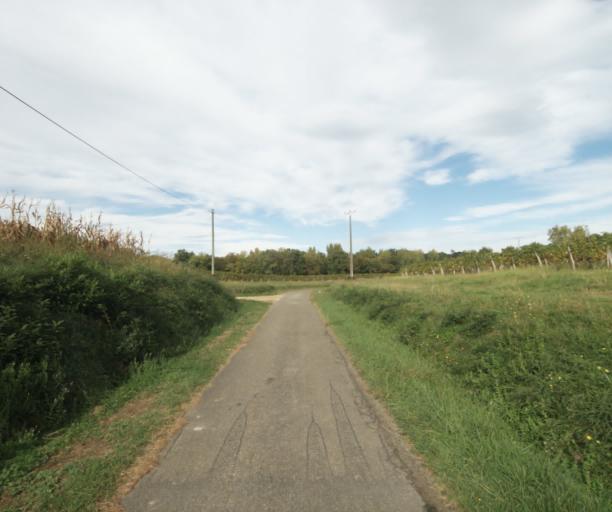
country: FR
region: Midi-Pyrenees
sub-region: Departement du Gers
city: Cazaubon
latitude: 43.8802
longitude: -0.1392
